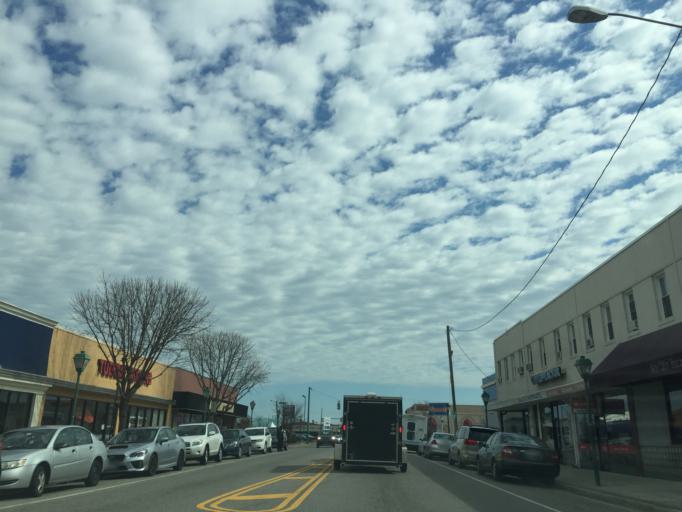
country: US
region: Virginia
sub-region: City of Norfolk
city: Norfolk
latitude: 36.8678
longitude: -76.2865
